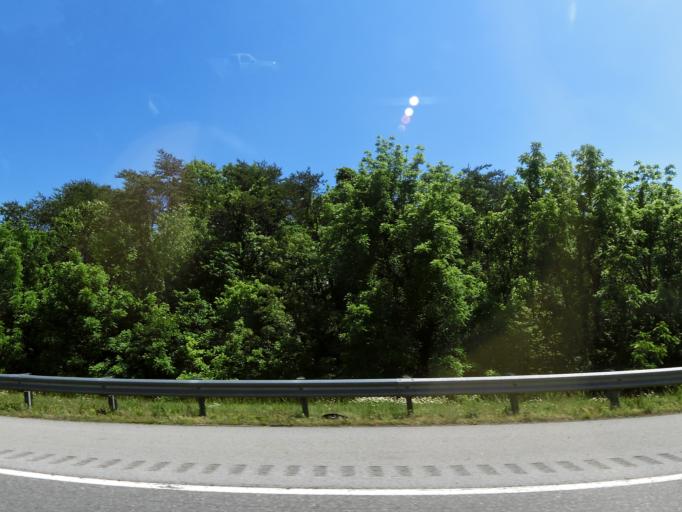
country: US
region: Tennessee
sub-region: Knox County
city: Mascot
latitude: 35.9965
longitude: -83.7010
